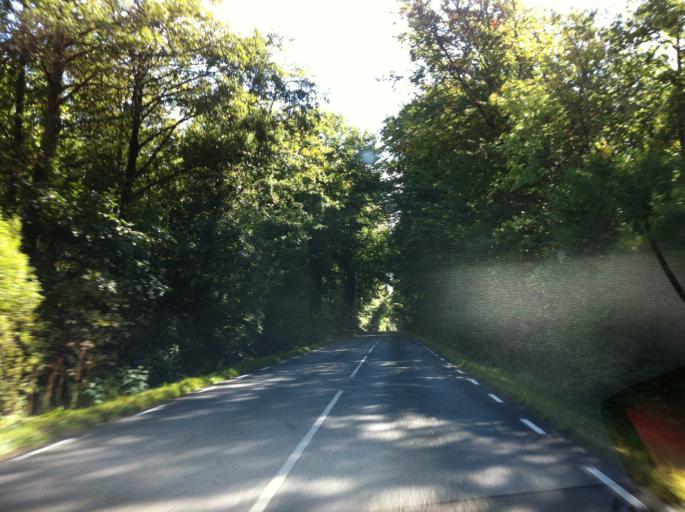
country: SE
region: Skane
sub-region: Kristianstads Kommun
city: Degeberga
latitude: 55.7822
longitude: 13.8786
